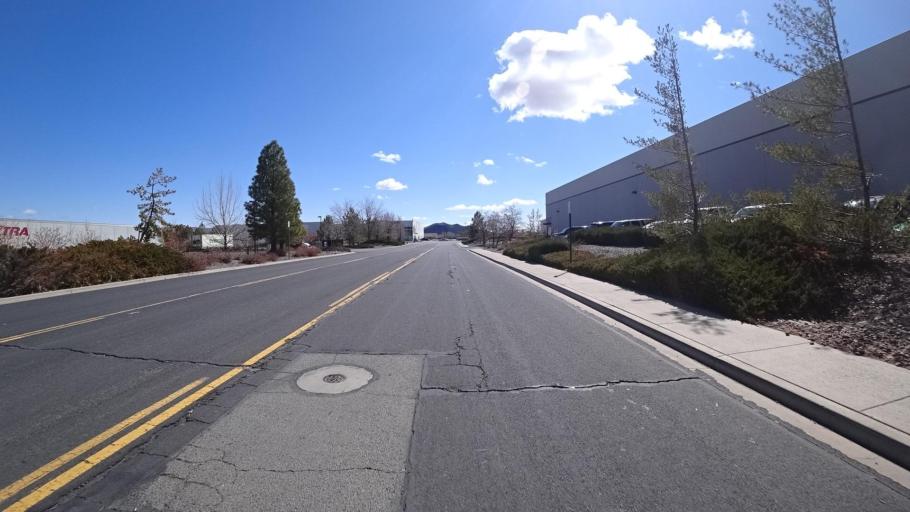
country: US
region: Nevada
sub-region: Washoe County
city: Lemmon Valley
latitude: 39.6467
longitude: -119.8620
